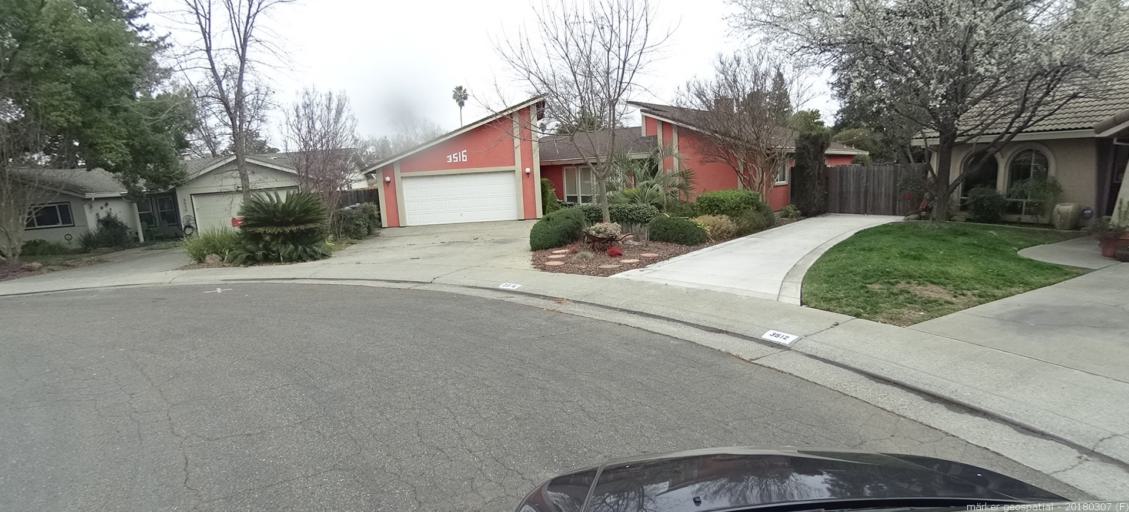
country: US
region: California
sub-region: Sacramento County
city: Carmichael
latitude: 38.6290
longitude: -121.3509
